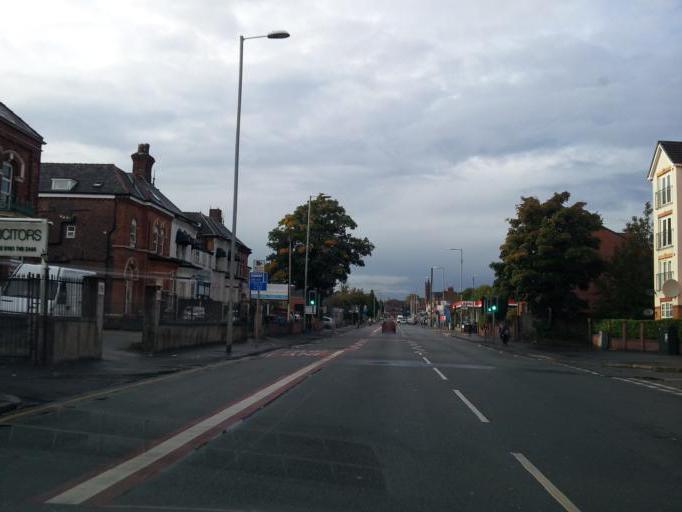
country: GB
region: England
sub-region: Manchester
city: Cheetham Hill
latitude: 53.5062
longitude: -2.2381
